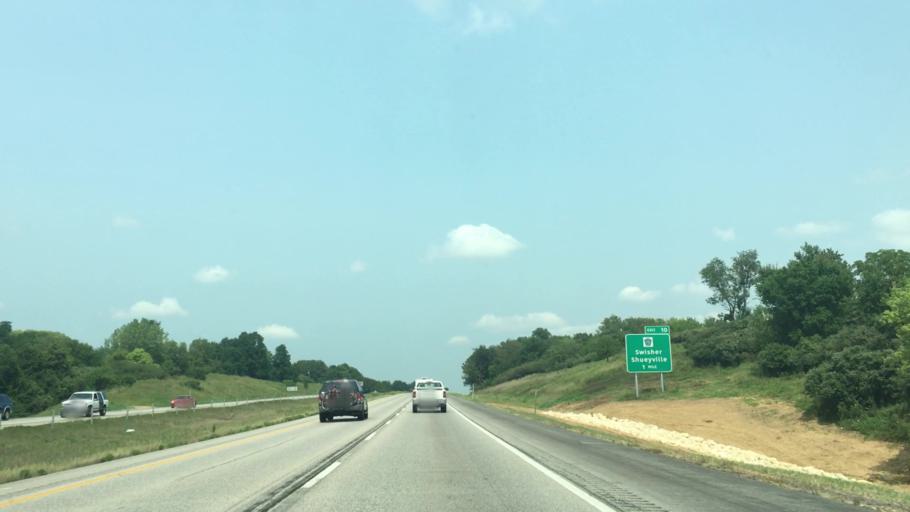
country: US
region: Iowa
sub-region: Linn County
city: Ely
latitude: 41.8294
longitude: -91.6599
